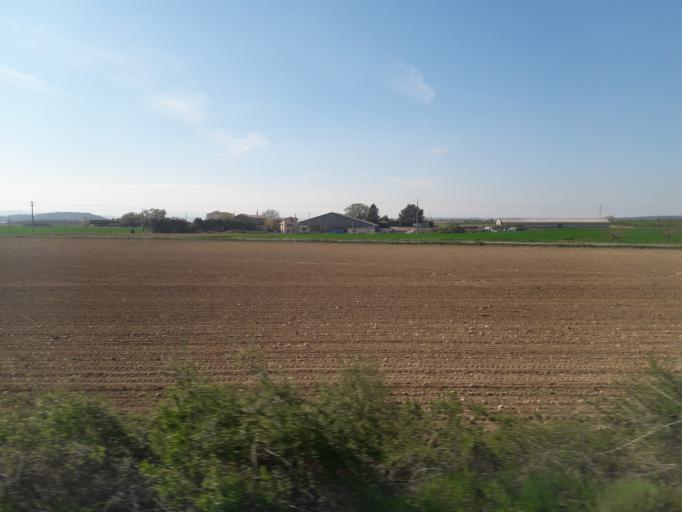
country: FR
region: Rhone-Alpes
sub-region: Departement de la Drome
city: Alixan
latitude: 45.0148
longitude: 5.0016
